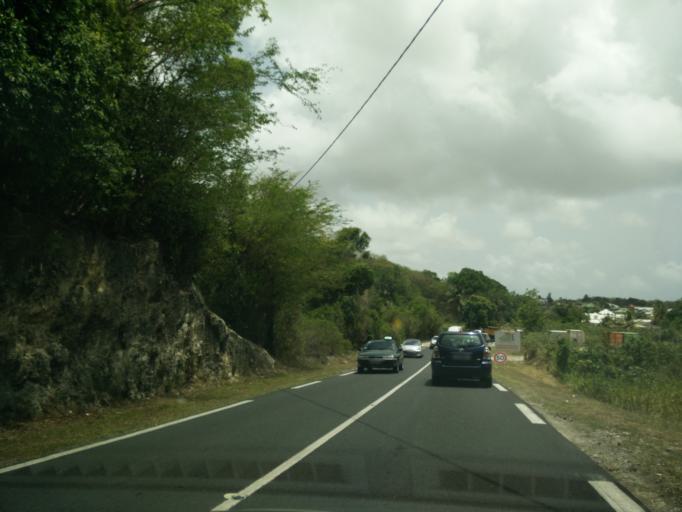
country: GP
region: Guadeloupe
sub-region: Guadeloupe
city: Petit-Canal
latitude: 16.3547
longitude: -61.4558
